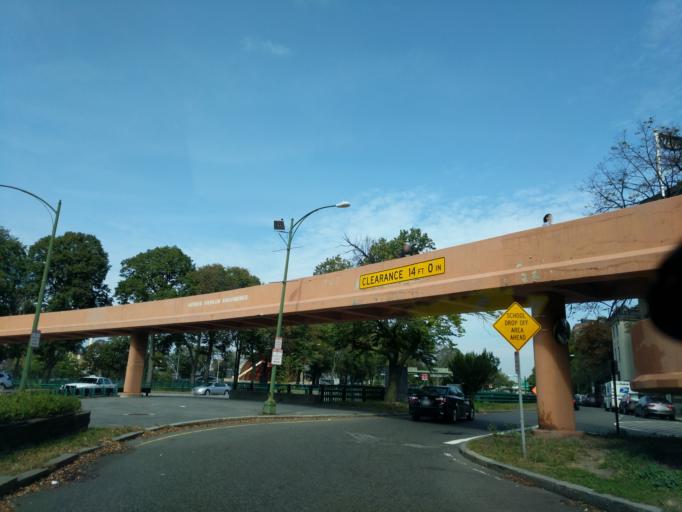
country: US
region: Massachusetts
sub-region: Suffolk County
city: Boston
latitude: 42.3558
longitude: -71.0732
